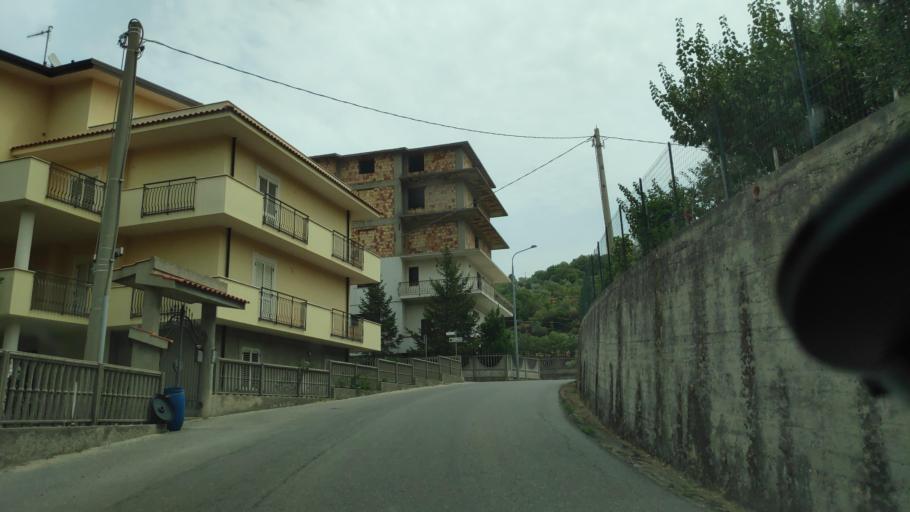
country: IT
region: Calabria
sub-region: Provincia di Catanzaro
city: Davoli
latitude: 38.6503
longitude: 16.4897
